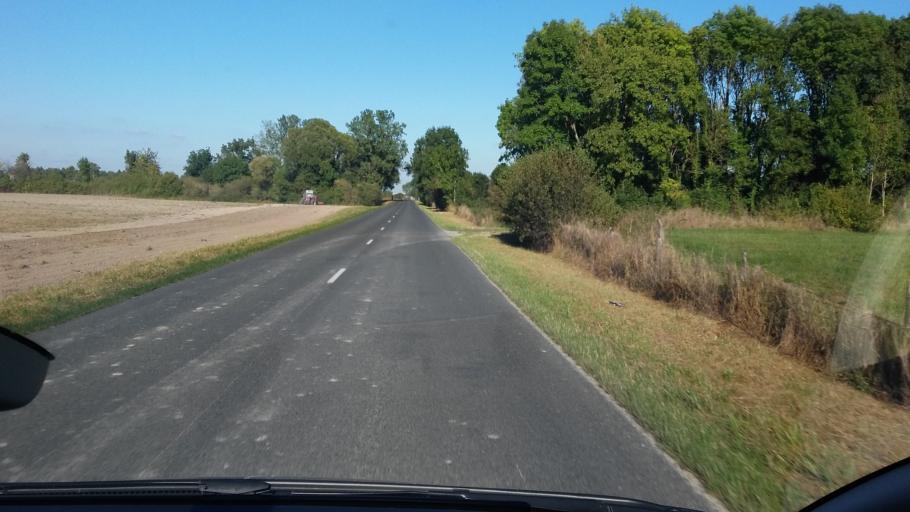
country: FR
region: Champagne-Ardenne
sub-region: Departement de la Marne
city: Connantre
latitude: 48.8084
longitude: 3.9143
